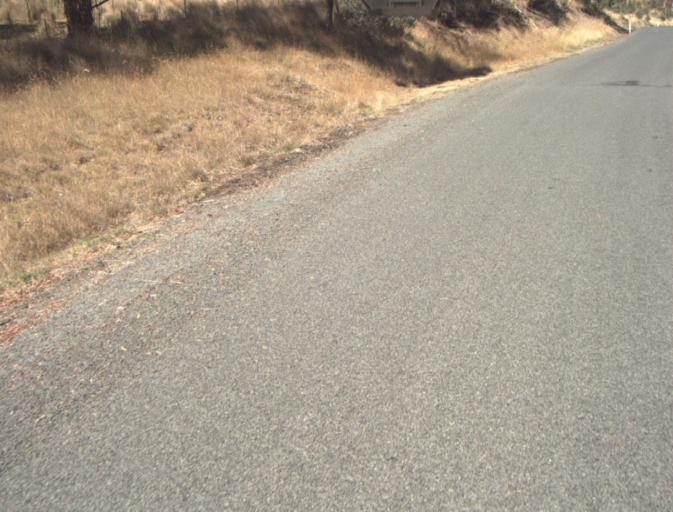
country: AU
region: Tasmania
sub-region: Launceston
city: Newstead
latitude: -41.3665
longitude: 147.3041
